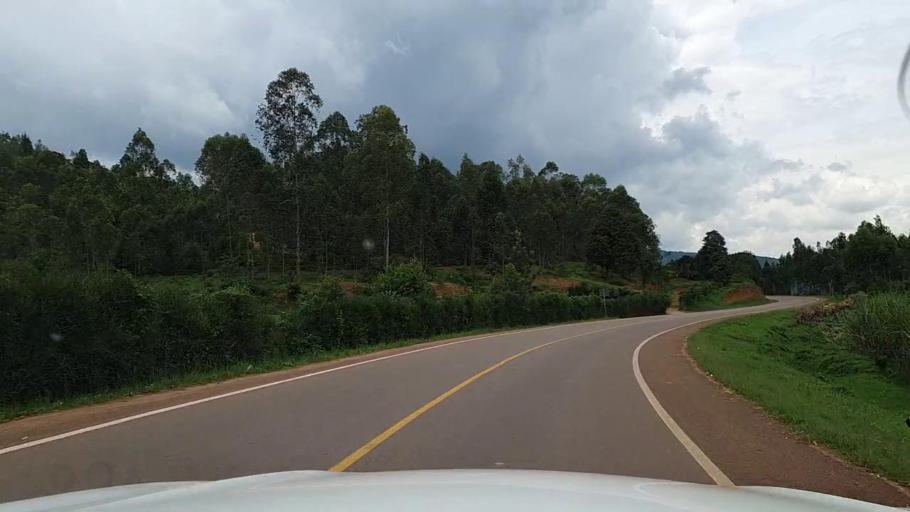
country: RW
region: Kigali
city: Kigali
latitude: -1.7772
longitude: 30.1276
